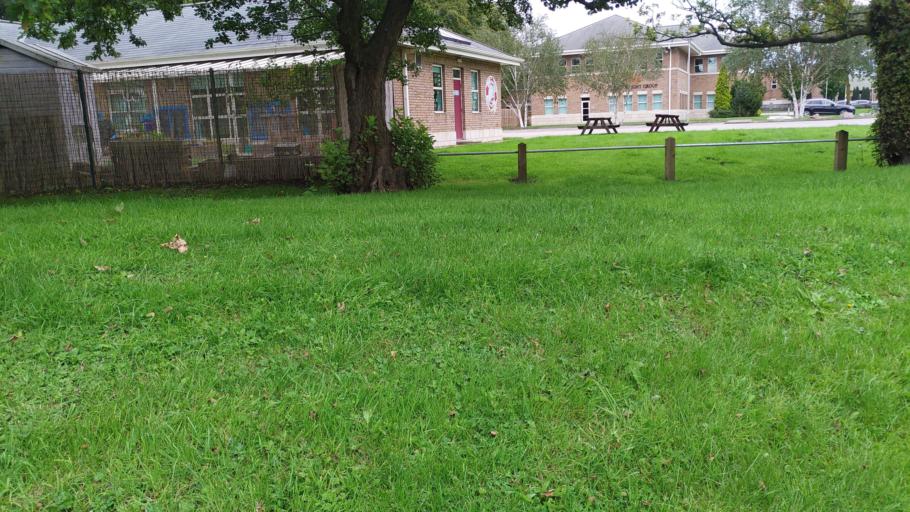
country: GB
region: England
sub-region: Lancashire
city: Clayton-le-Woods
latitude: 53.7183
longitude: -2.6420
